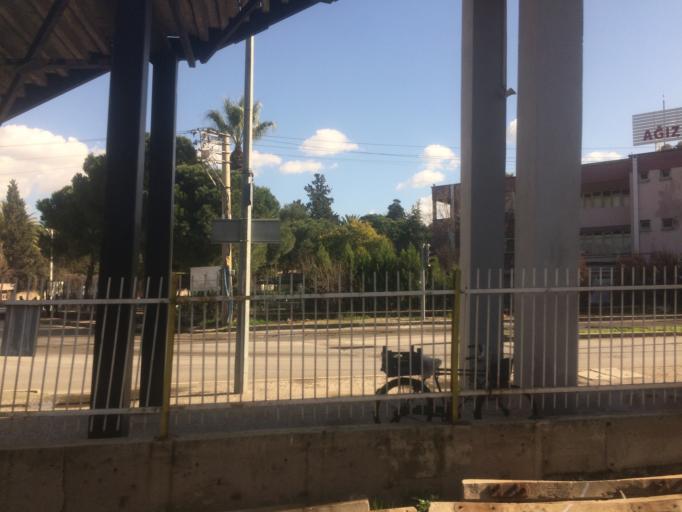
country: TR
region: Izmir
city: Buca
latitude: 38.4402
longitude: 27.1735
